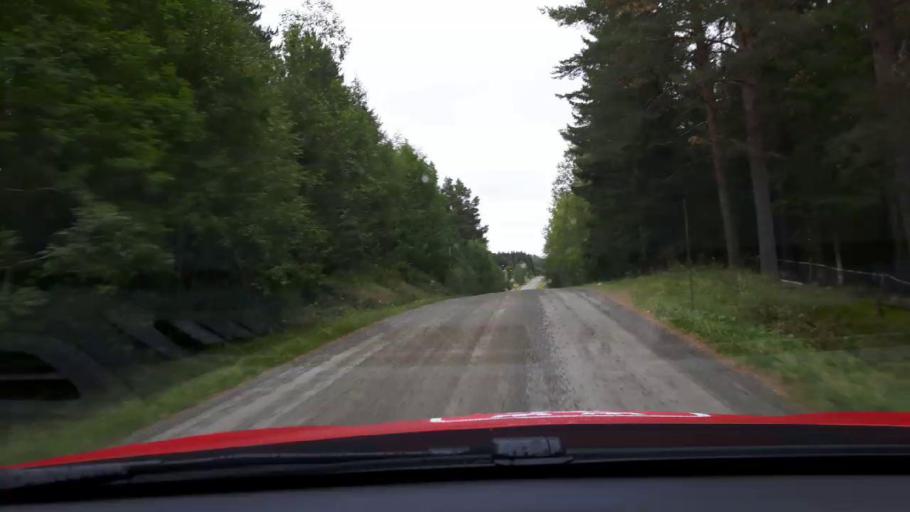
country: SE
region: Jaemtland
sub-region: Bergs Kommun
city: Hoverberg
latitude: 62.8650
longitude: 14.2979
